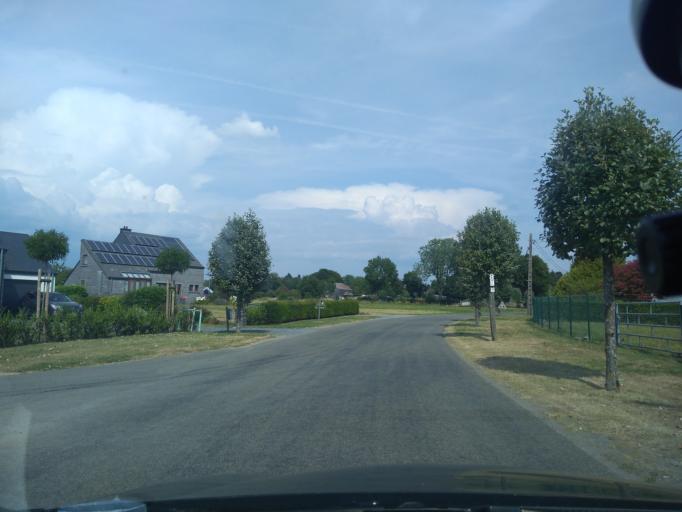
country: BE
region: Wallonia
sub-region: Province du Luxembourg
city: Bertogne
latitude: 50.1578
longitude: 5.6761
